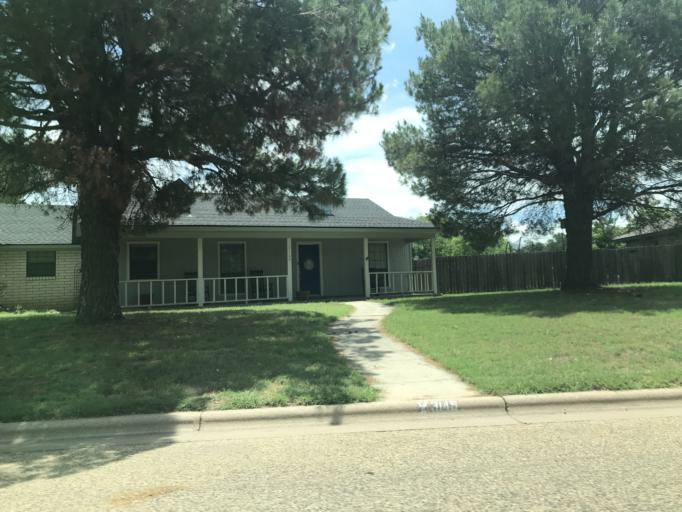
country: US
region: Texas
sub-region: Taylor County
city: Abilene
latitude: 32.4872
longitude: -99.6852
